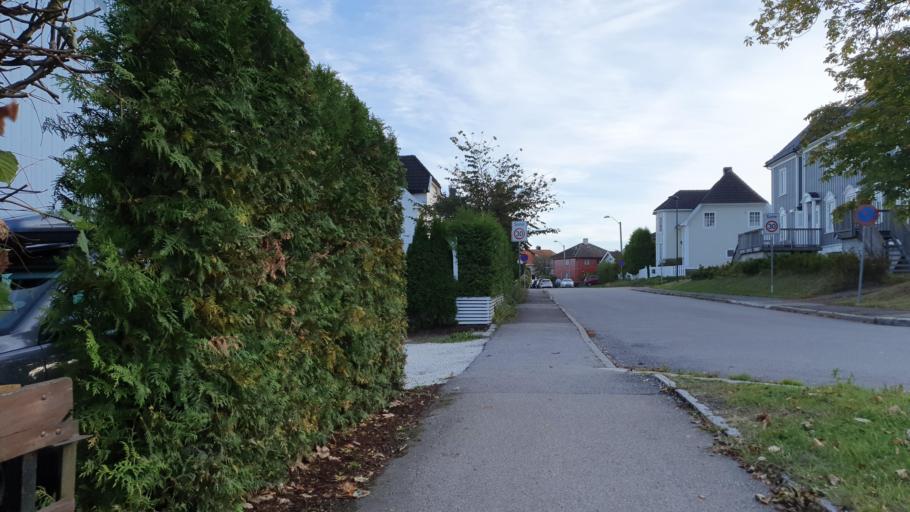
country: NO
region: Vestfold
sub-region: Tonsberg
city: Tonsberg
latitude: 59.2707
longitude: 10.4232
